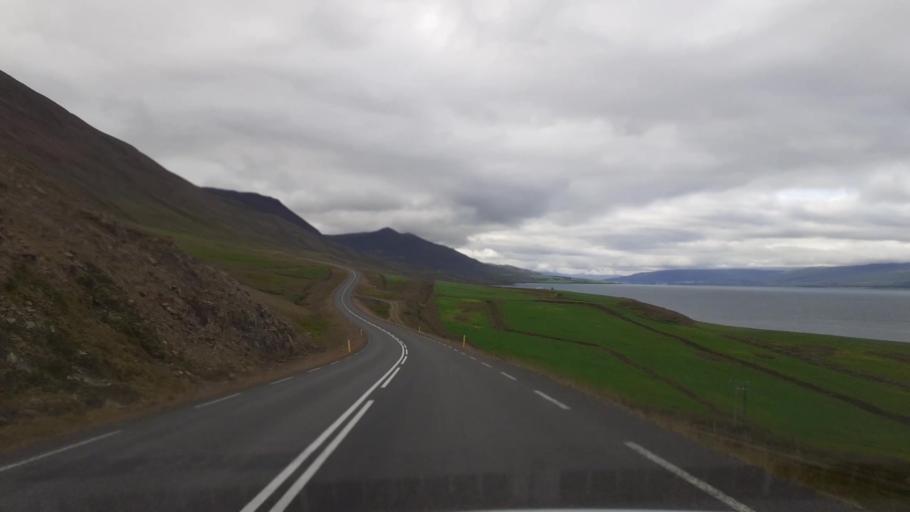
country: IS
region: Northeast
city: Akureyri
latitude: 65.8680
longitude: -18.0758
